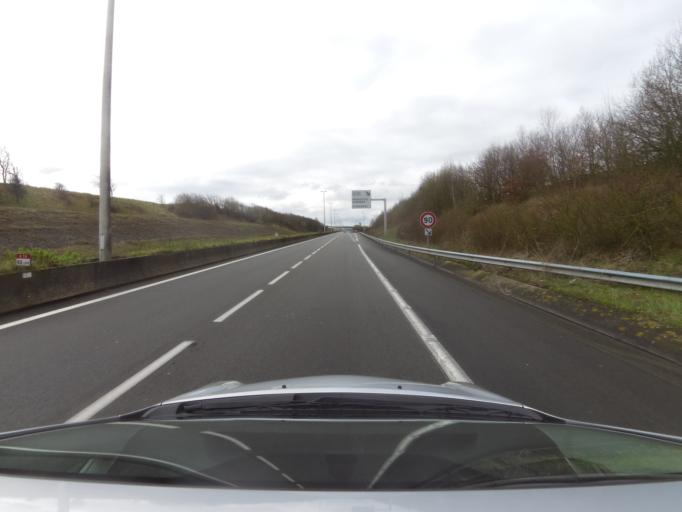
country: FR
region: Nord-Pas-de-Calais
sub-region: Departement du Pas-de-Calais
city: Marquise
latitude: 50.8308
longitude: 1.7021
